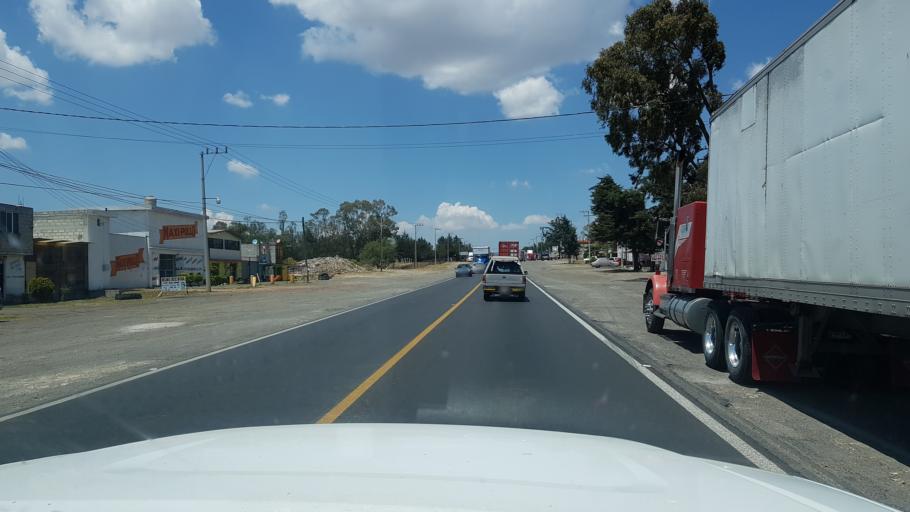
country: MX
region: Hidalgo
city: Calpulalpan
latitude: 19.5885
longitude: -98.5514
